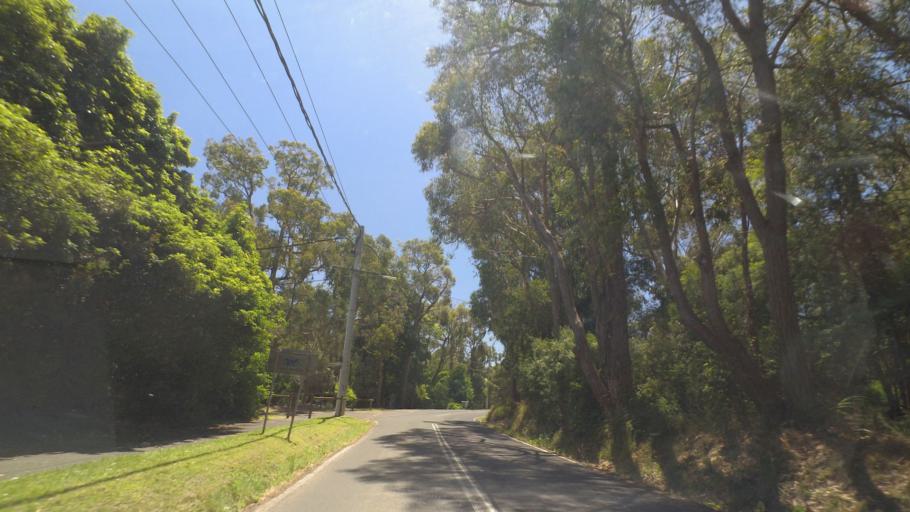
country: AU
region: Victoria
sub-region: Yarra Ranges
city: Montrose
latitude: -37.8176
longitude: 145.3409
